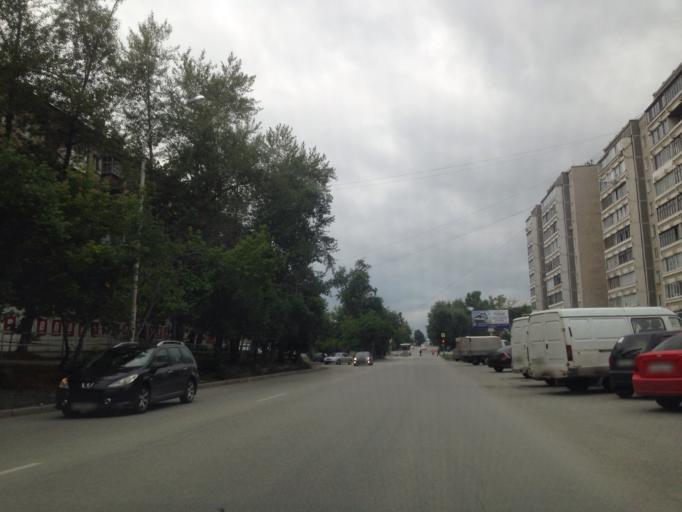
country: RU
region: Sverdlovsk
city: Yekaterinburg
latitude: 56.8321
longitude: 60.6941
